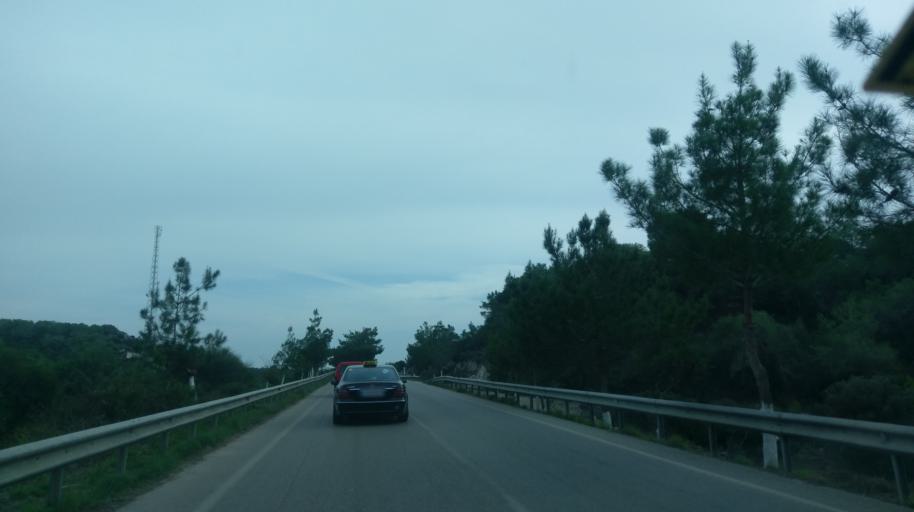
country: CY
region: Ammochostos
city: Leonarisso
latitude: 35.4466
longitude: 34.1347
